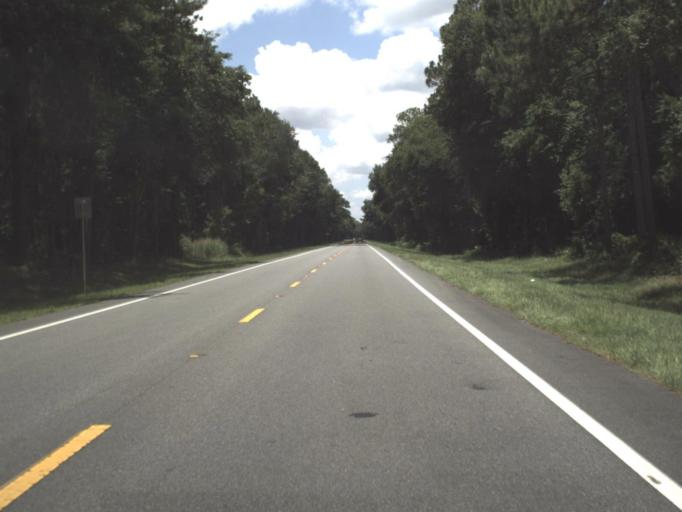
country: US
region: Florida
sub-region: Alachua County
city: Gainesville
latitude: 29.6879
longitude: -82.2281
